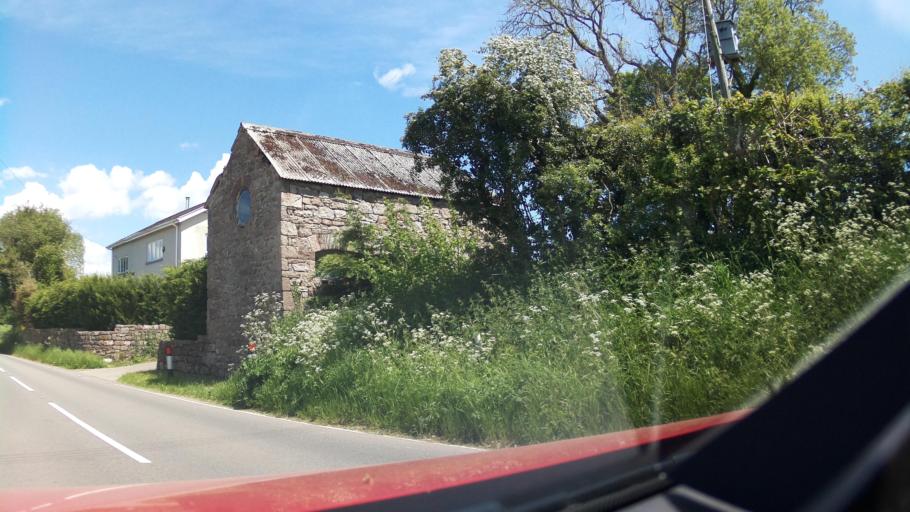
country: GB
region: Wales
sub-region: Monmouthshire
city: Mitchel Troy
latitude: 51.7419
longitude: -2.7286
